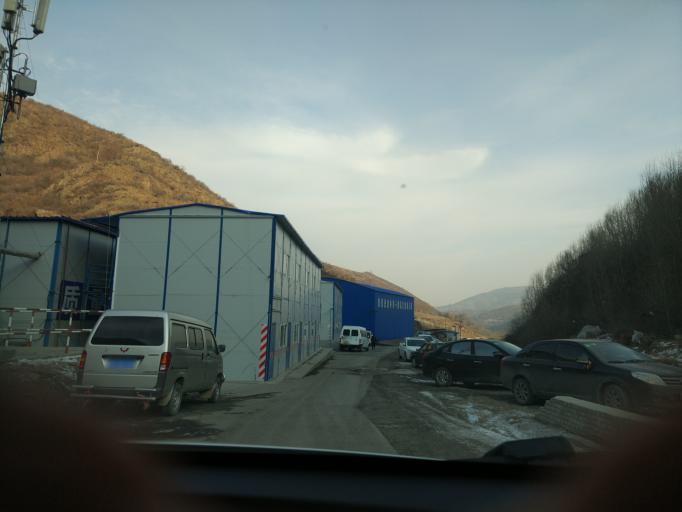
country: CN
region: Hebei
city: Xiwanzi
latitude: 40.8164
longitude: 115.4508
